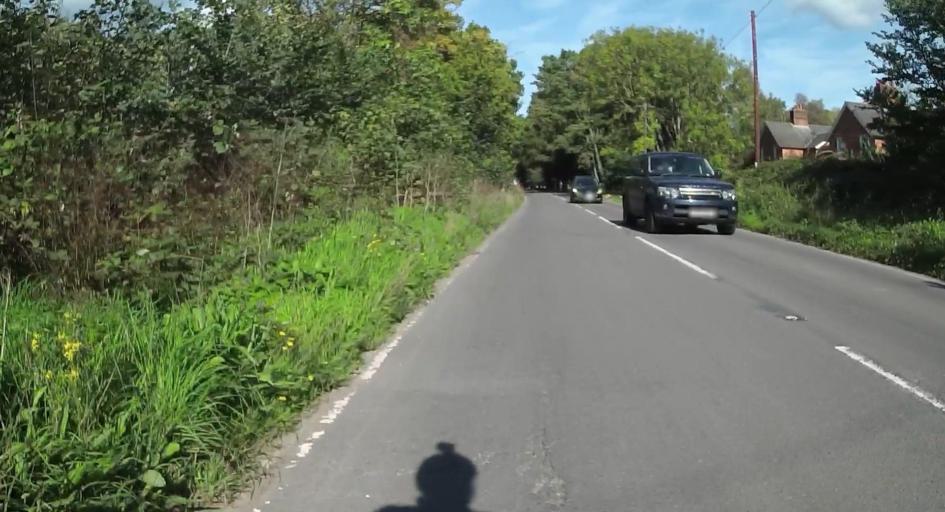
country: GB
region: England
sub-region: Surrey
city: Chertsey
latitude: 51.3830
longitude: -0.5251
